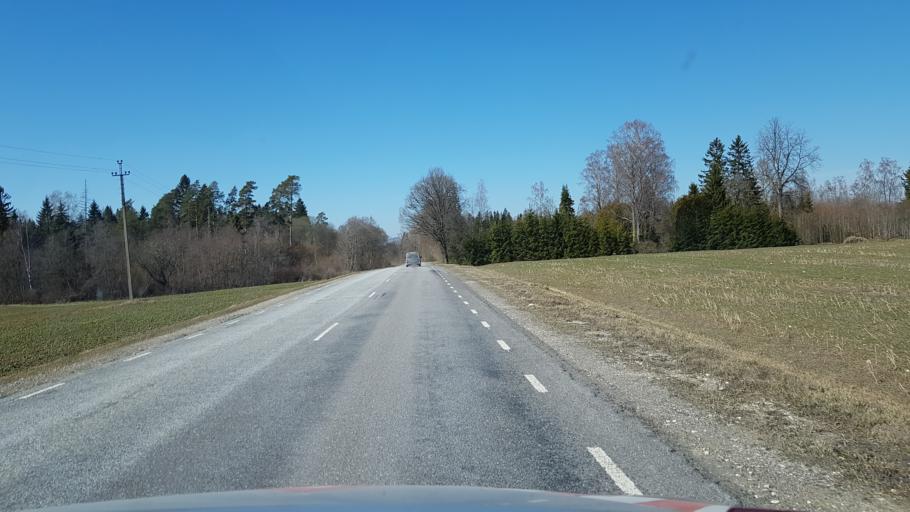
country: EE
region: Laeaene-Virumaa
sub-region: Vaeike-Maarja vald
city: Vaike-Maarja
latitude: 59.1513
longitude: 26.2216
